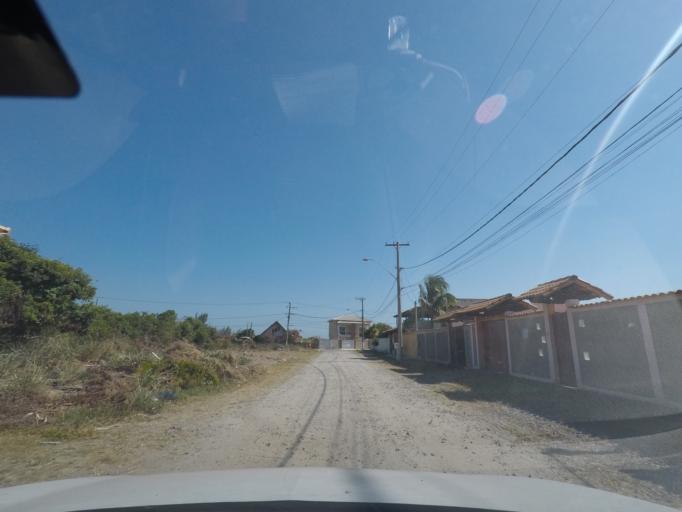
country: BR
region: Rio de Janeiro
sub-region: Marica
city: Marica
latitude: -22.9685
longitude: -42.9083
